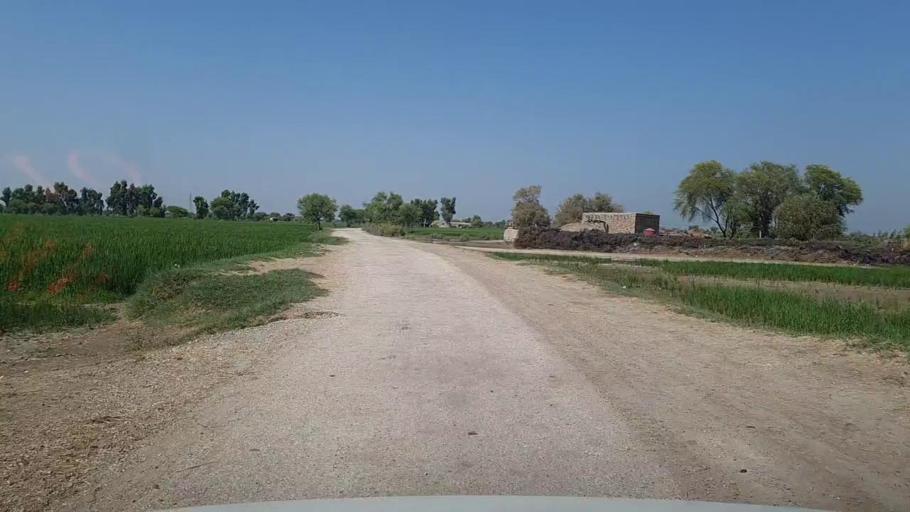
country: PK
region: Sindh
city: Kandhkot
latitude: 28.3292
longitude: 69.3672
